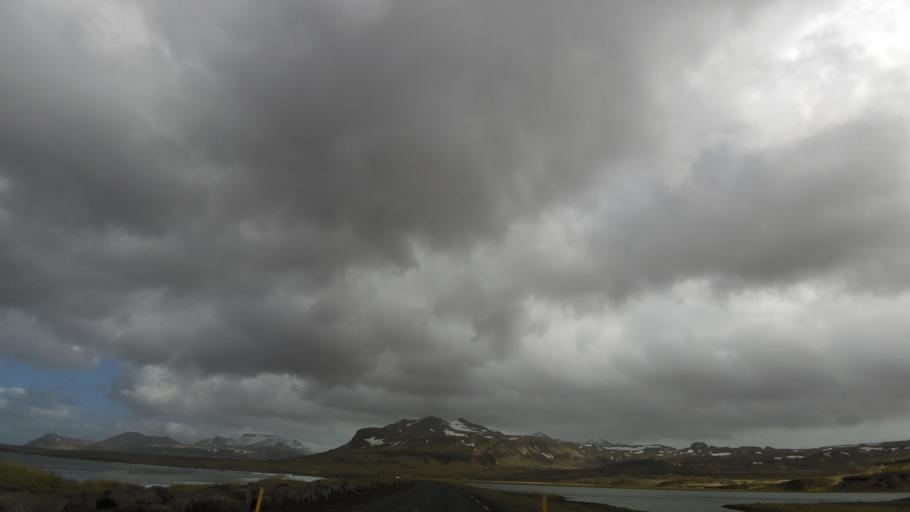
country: IS
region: West
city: Olafsvik
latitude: 64.8893
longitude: -23.6431
